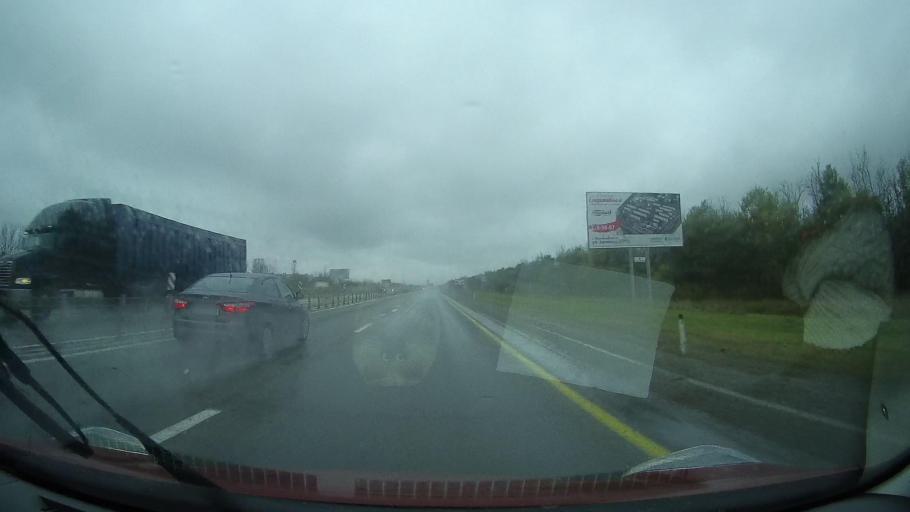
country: RU
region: Stavropol'skiy
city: Nevinnomyssk
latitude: 44.6404
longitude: 41.9705
